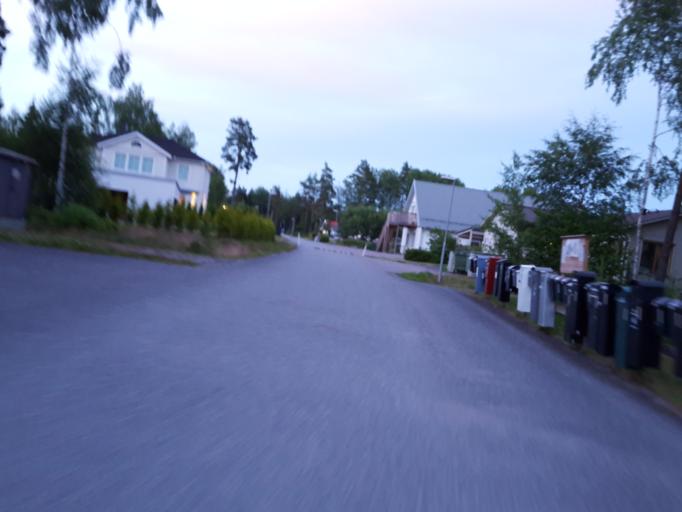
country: SE
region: Uppsala
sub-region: Uppsala Kommun
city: Uppsala
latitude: 59.7765
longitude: 17.5939
